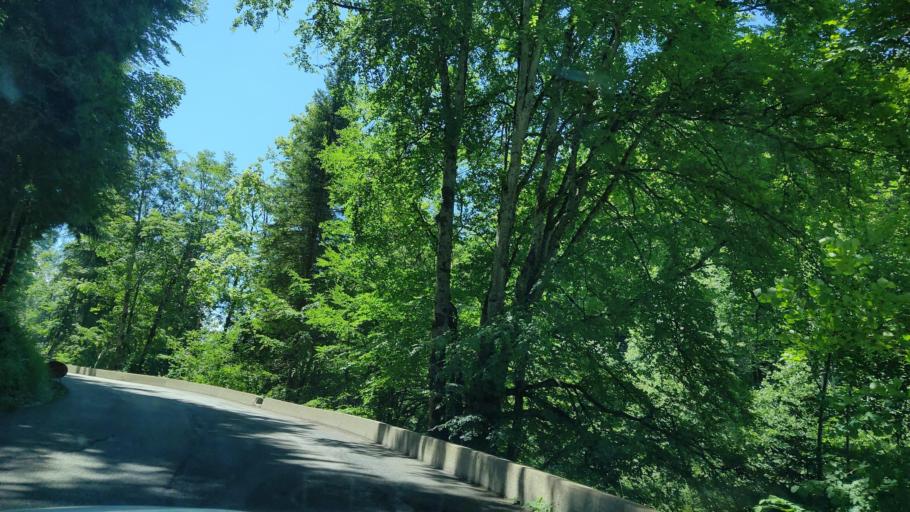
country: FR
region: Rhone-Alpes
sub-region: Departement de la Haute-Savoie
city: Praz-sur-Arly
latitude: 45.8390
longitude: 6.5080
